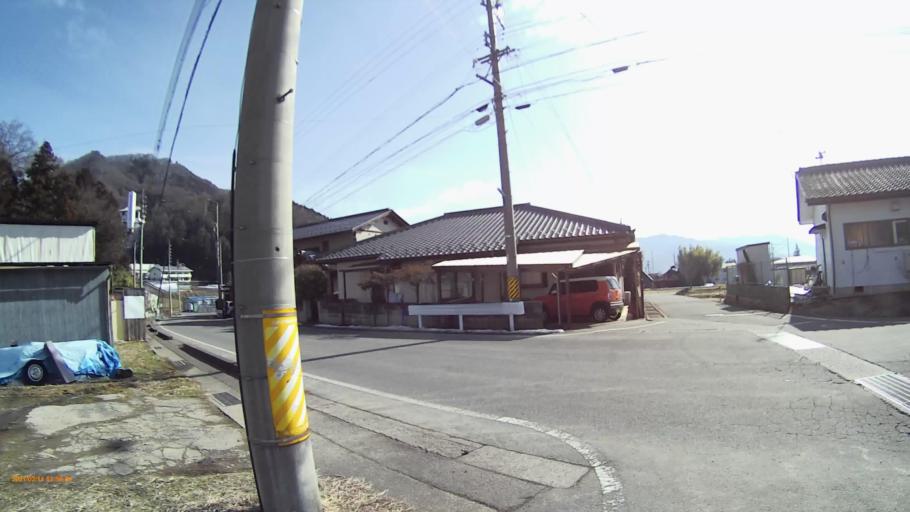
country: JP
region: Nagano
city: Nakano
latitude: 36.7477
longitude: 138.3793
